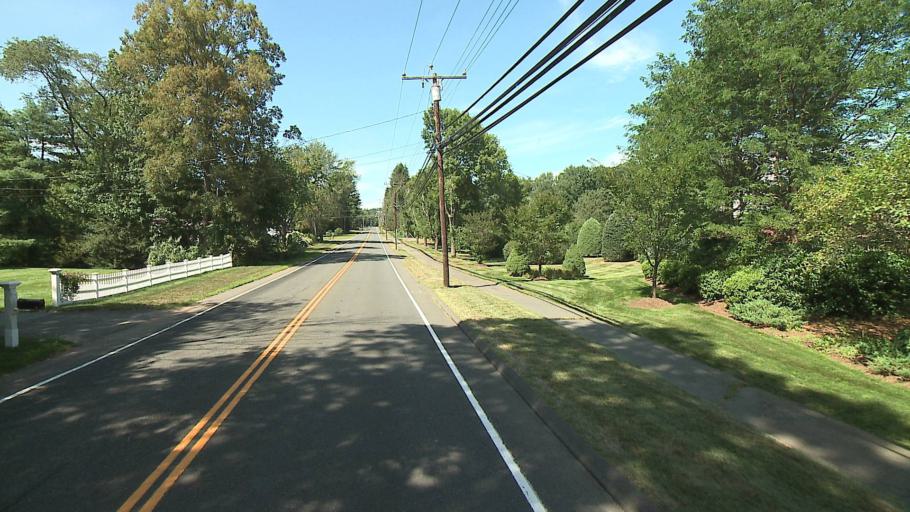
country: US
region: Connecticut
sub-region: Hartford County
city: Canton Valley
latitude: 41.7779
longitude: -72.8634
